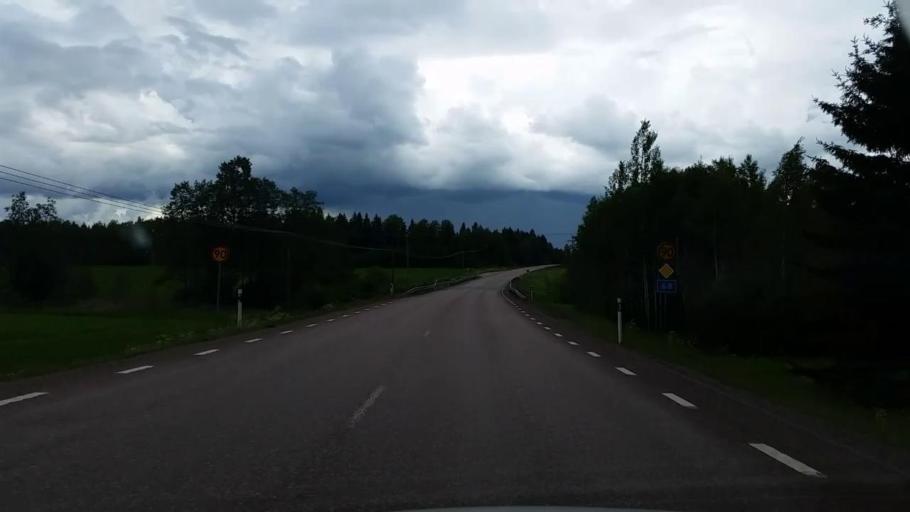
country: SE
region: Gaevleborg
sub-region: Hofors Kommun
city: Hofors
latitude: 60.5159
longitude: 16.4376
